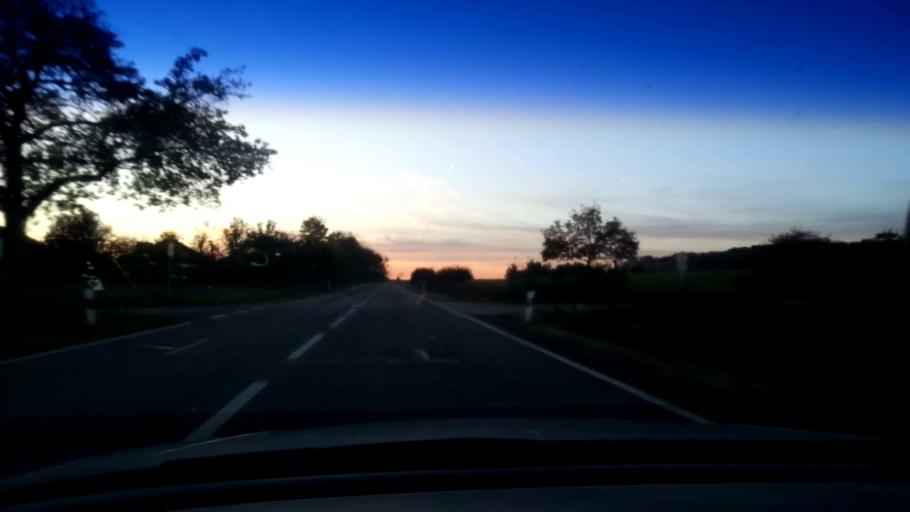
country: DE
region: Bavaria
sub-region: Upper Franconia
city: Litzendorf
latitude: 49.8706
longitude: 11.0276
